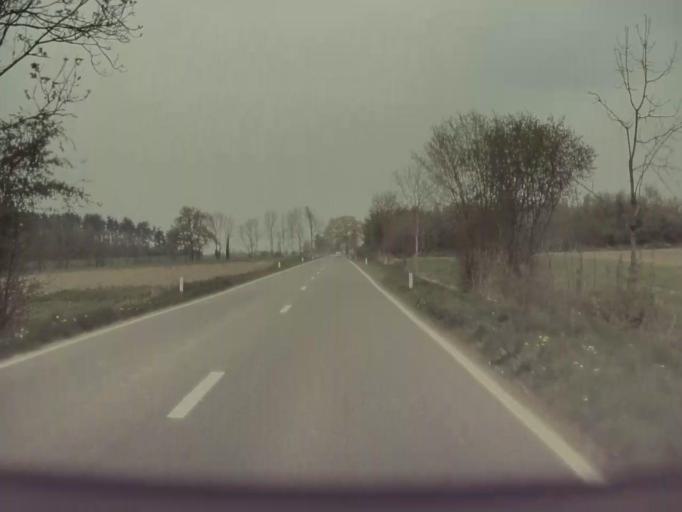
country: BE
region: Wallonia
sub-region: Province de Liege
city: Ferrieres
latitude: 50.4163
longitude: 5.5787
